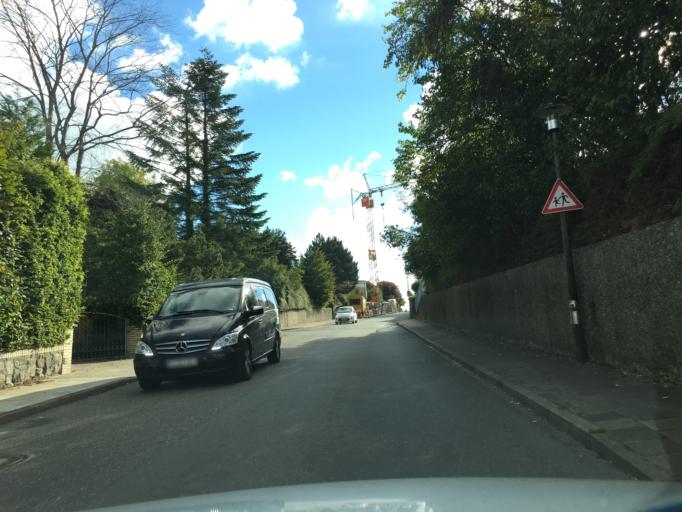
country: DE
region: Schleswig-Holstein
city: Laboe
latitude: 54.4027
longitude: 10.2219
